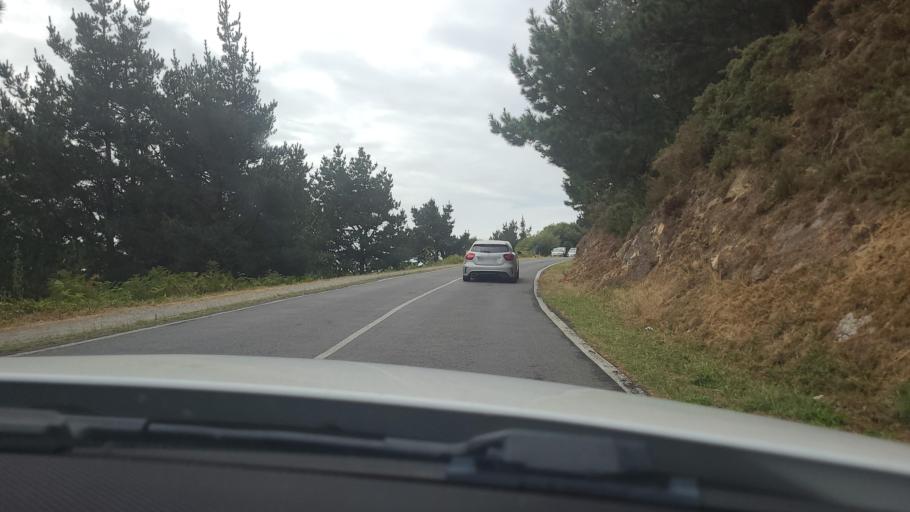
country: ES
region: Galicia
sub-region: Provincia da Coruna
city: Fisterra
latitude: 42.8989
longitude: -9.2632
